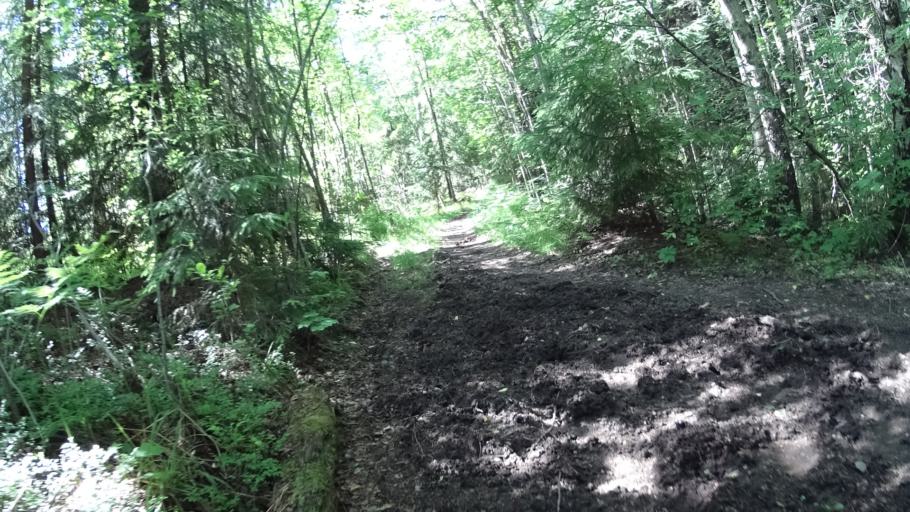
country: FI
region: Uusimaa
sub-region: Helsinki
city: Kilo
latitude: 60.2937
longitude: 24.8240
